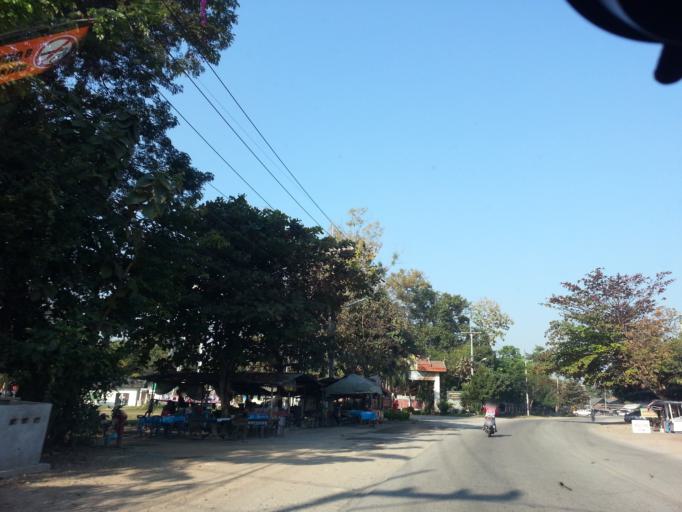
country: TH
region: Chiang Mai
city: San Sai
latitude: 18.8780
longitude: 99.0381
